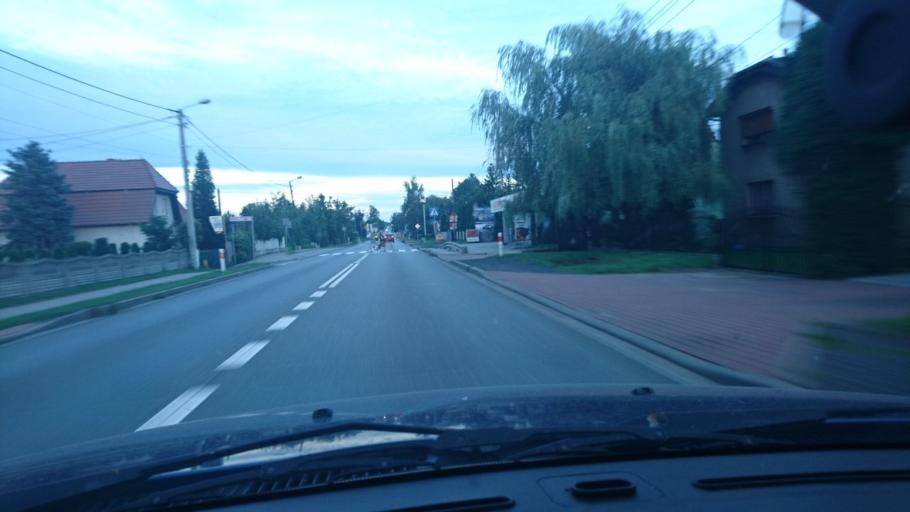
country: PL
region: Silesian Voivodeship
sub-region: Powiat tarnogorski
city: Tarnowskie Gory
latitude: 50.4698
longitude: 18.8076
